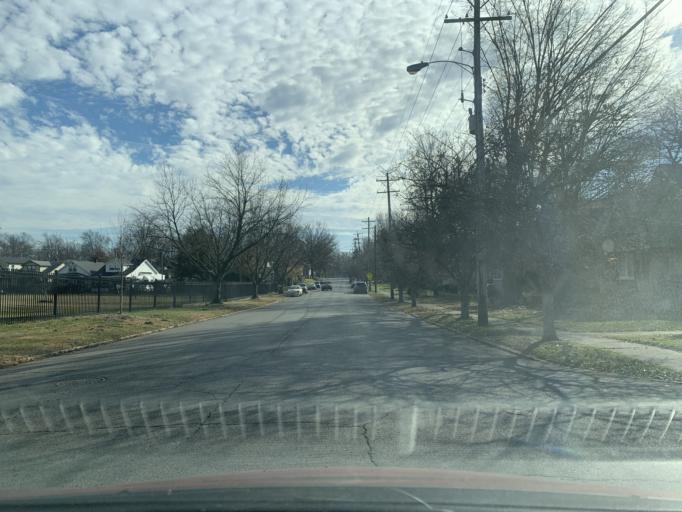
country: US
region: Kentucky
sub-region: Jefferson County
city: Saint Matthews
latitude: 38.2513
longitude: -85.6828
